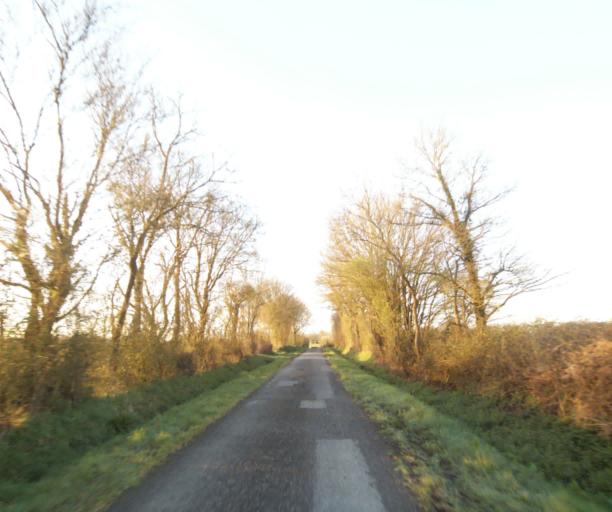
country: FR
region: Pays de la Loire
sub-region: Departement de la Loire-Atlantique
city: Bouvron
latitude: 47.4275
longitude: -1.8832
